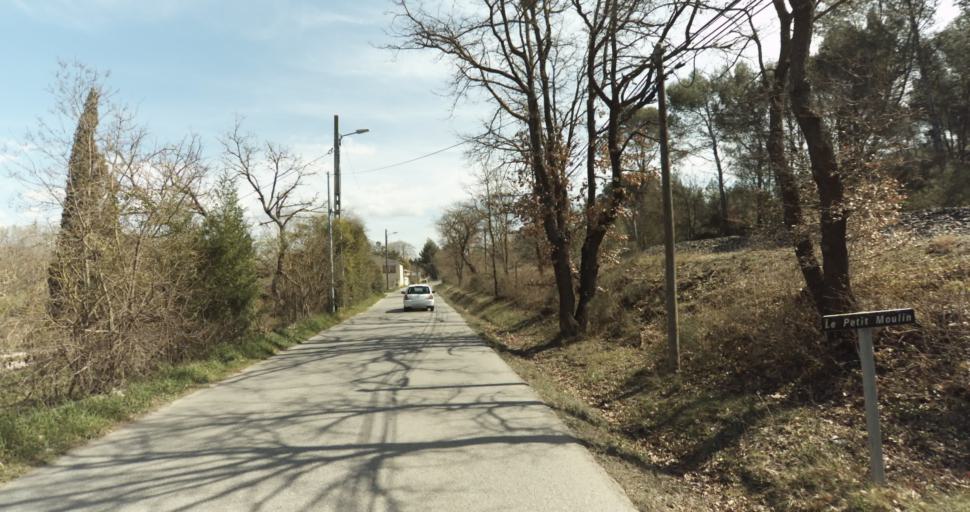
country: FR
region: Provence-Alpes-Cote d'Azur
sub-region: Departement des Bouches-du-Rhone
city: Ventabren
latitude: 43.5037
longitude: 5.3411
